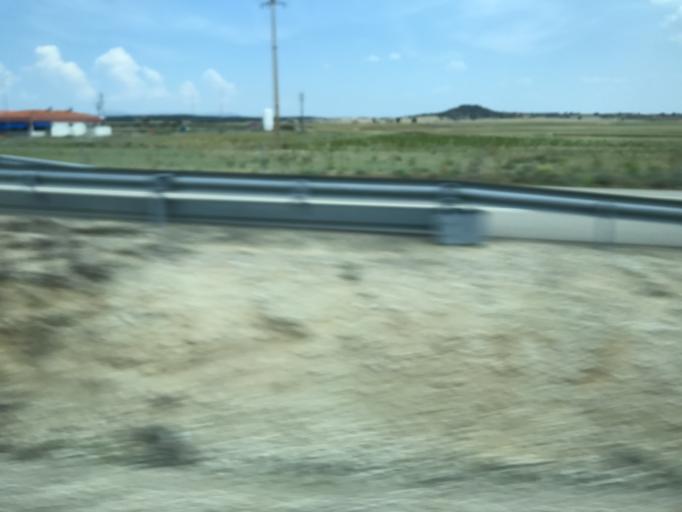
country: ES
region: Castille and Leon
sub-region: Provincia de Burgos
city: Oquillas
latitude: 41.8235
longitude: -3.7051
